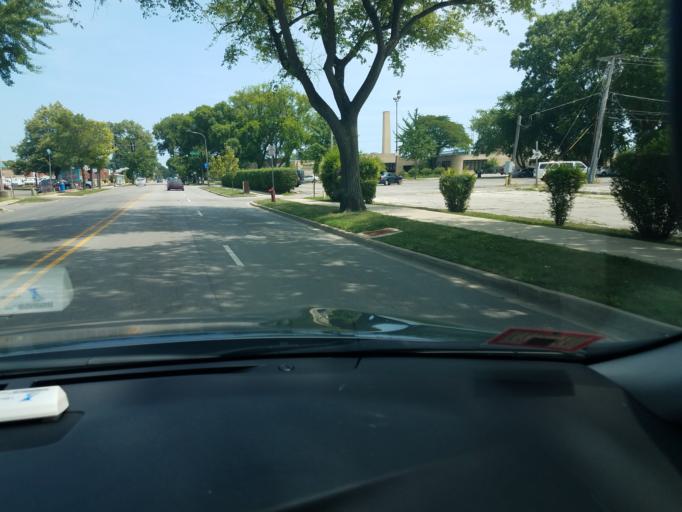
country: US
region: Illinois
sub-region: Cook County
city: Evanston
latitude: 42.0410
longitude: -87.7050
